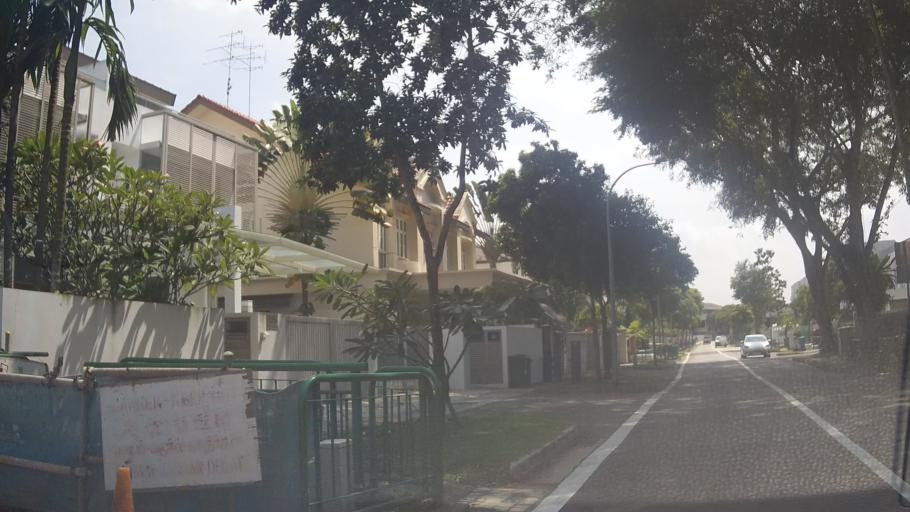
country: SG
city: Singapore
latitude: 1.3221
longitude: 103.7977
